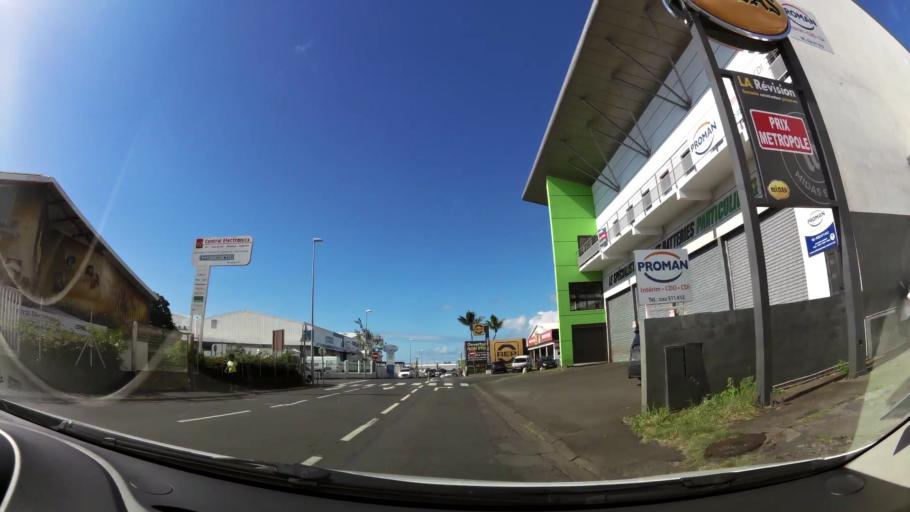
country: RE
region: Reunion
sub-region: Reunion
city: Saint-Denis
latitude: -20.8920
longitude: 55.4951
